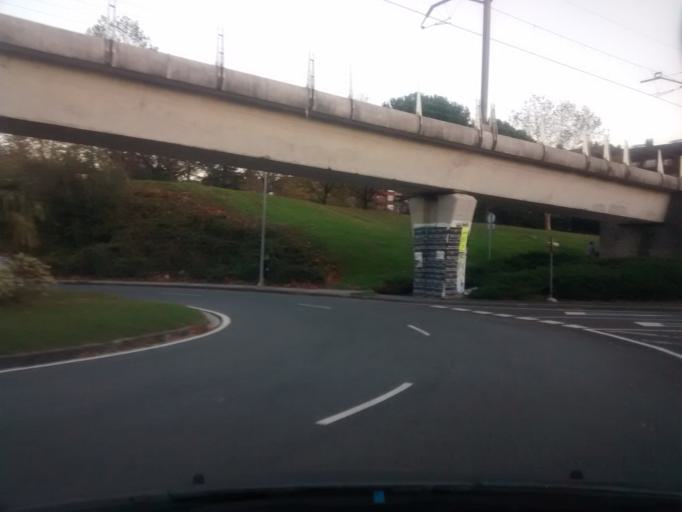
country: ES
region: Basque Country
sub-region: Provincia de Guipuzcoa
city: Lasarte
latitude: 43.2749
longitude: -2.0216
